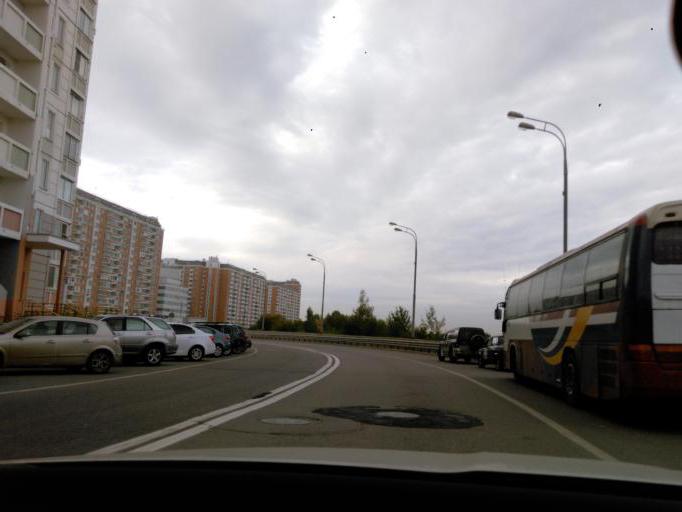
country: RU
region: Moscow
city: Severnyy
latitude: 55.9267
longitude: 37.5398
